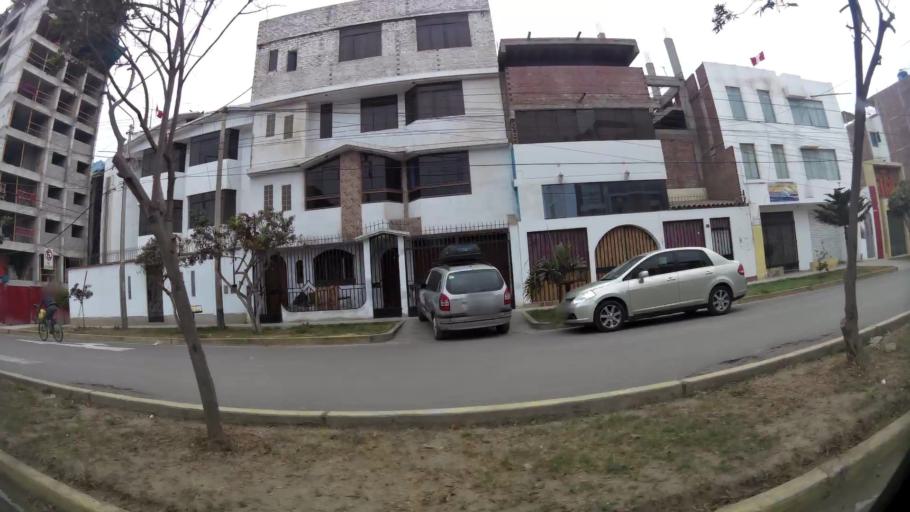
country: PE
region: La Libertad
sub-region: Provincia de Trujillo
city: Trujillo
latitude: -8.1215
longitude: -79.0474
